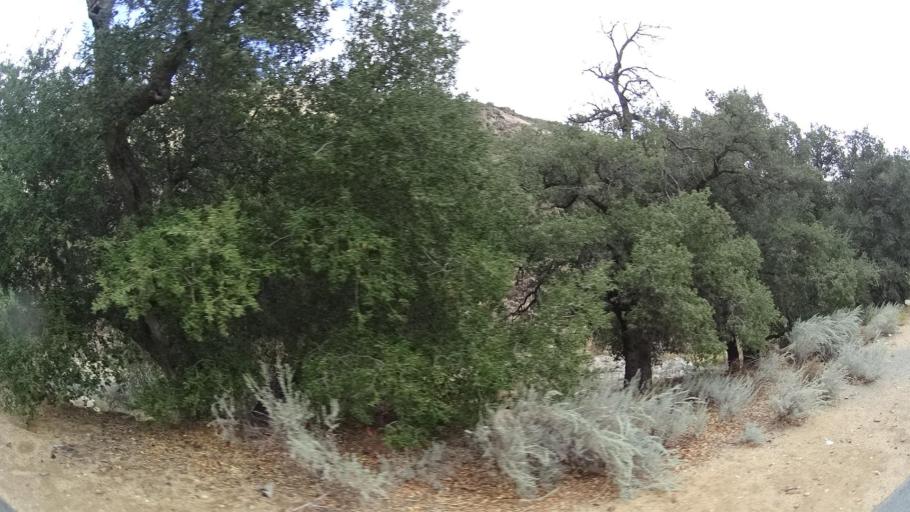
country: US
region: California
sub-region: San Diego County
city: Pine Valley
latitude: 32.7690
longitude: -116.4505
